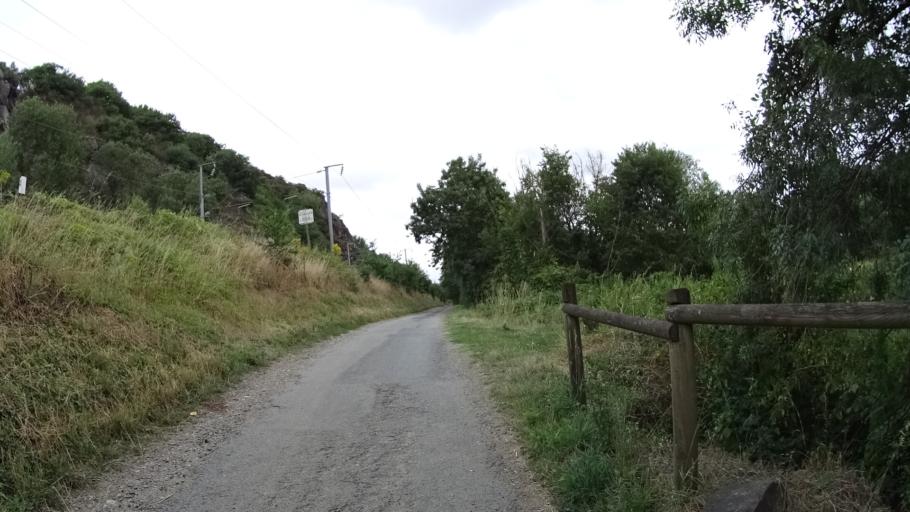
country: FR
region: Pays de la Loire
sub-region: Departement de la Loire-Atlantique
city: Le Cellier
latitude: 47.3060
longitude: -1.3602
